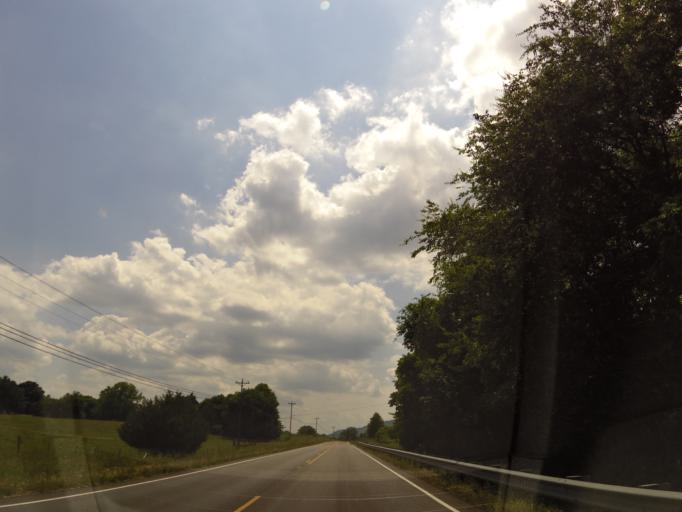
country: US
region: Tennessee
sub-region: Bledsoe County
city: Pikeville
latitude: 35.5692
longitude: -85.2379
